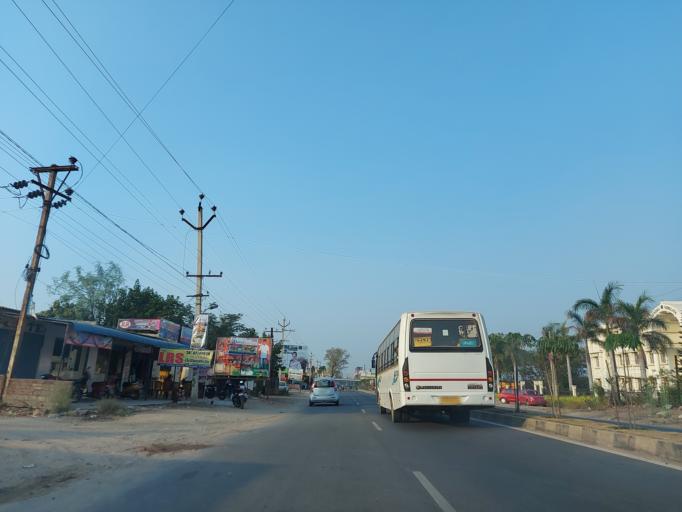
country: IN
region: Telangana
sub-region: Rangareddi
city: Balapur
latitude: 17.1996
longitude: 78.4757
